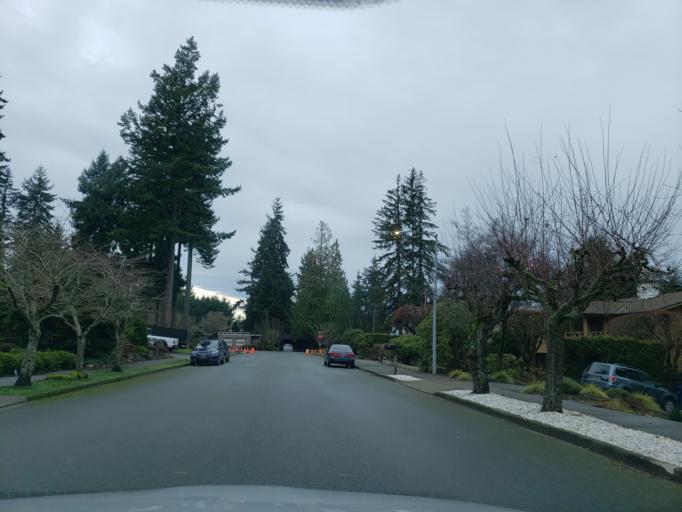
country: US
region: Washington
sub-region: Snohomish County
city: Meadowdale
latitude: 47.8310
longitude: -122.3510
